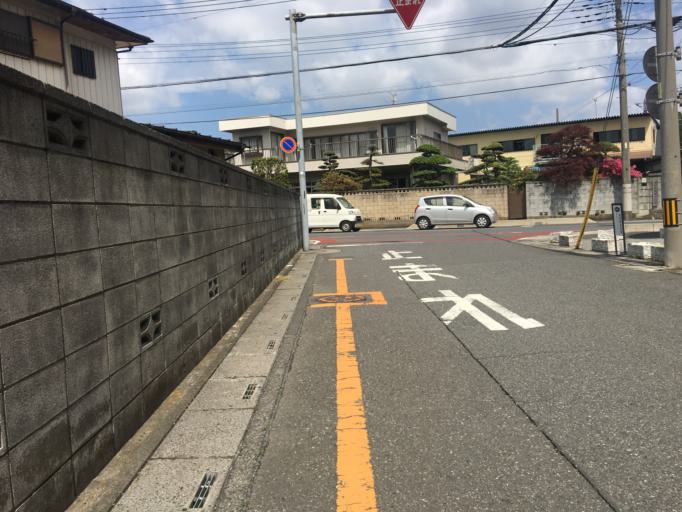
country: JP
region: Saitama
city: Yono
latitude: 35.8838
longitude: 139.6140
